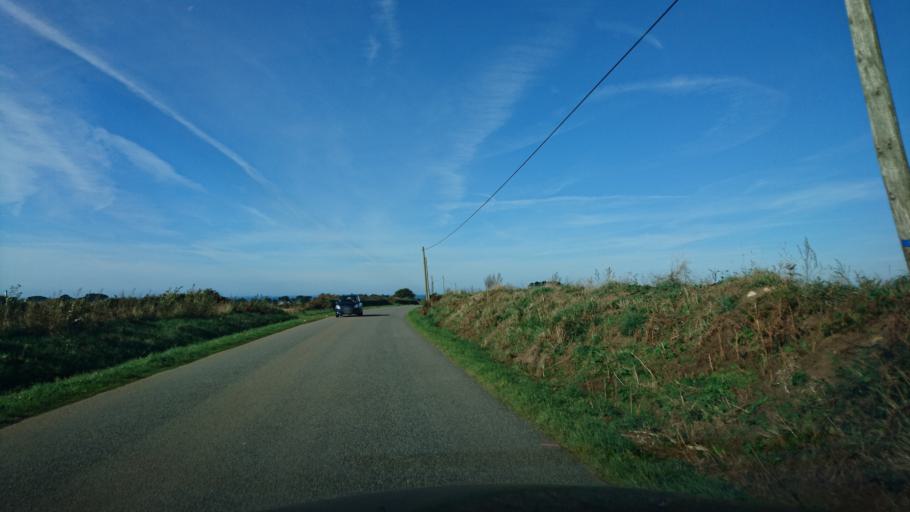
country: FR
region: Brittany
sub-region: Departement du Finistere
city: Plouarzel
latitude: 48.4280
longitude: -4.7528
